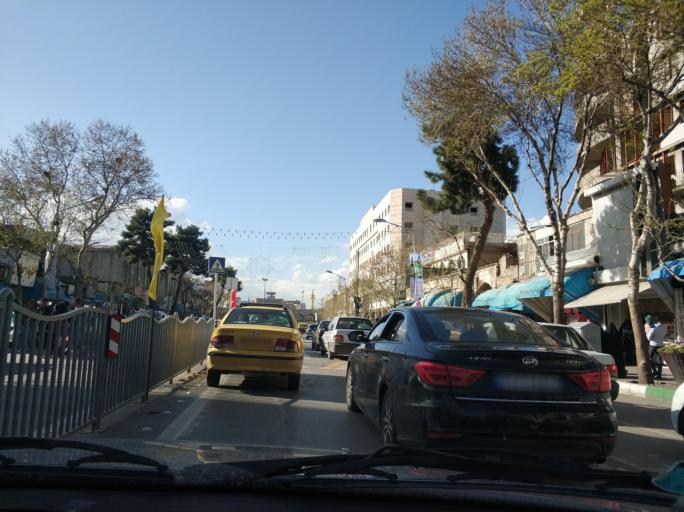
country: IR
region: Razavi Khorasan
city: Mashhad
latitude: 36.2846
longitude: 59.6204
